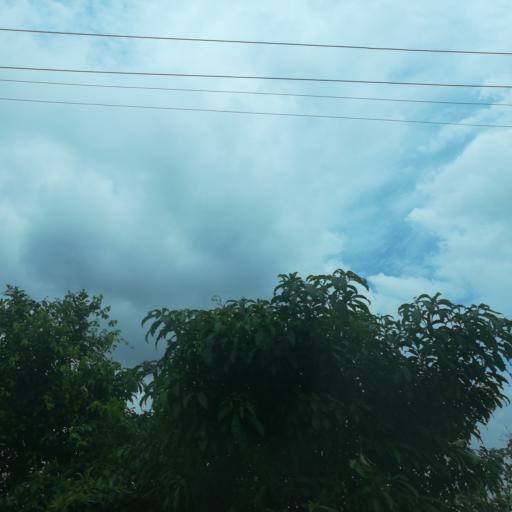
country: NG
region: Ogun
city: Odogbolu
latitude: 6.6672
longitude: 3.7100
